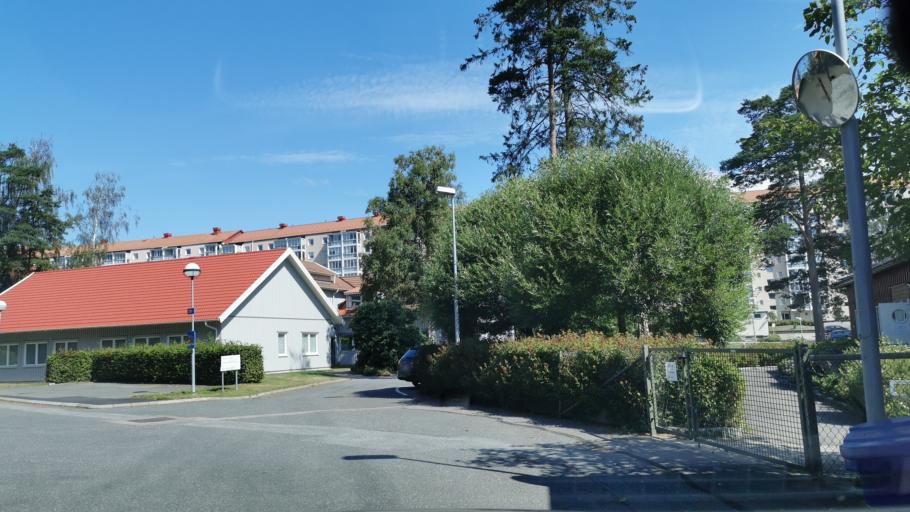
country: SE
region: Vaestra Goetaland
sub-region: Goteborg
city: Majorna
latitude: 57.6612
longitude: 11.9174
